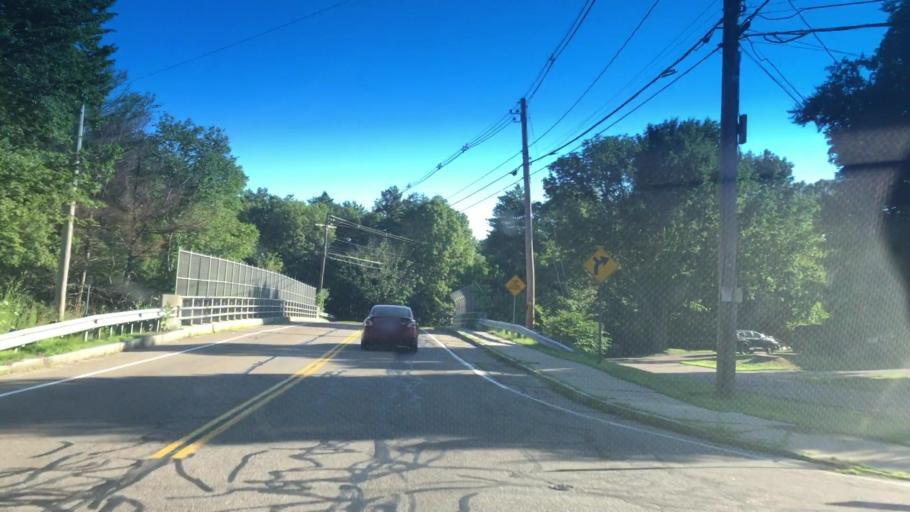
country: US
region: Massachusetts
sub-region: Norfolk County
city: Walpole
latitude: 42.1358
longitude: -71.2841
